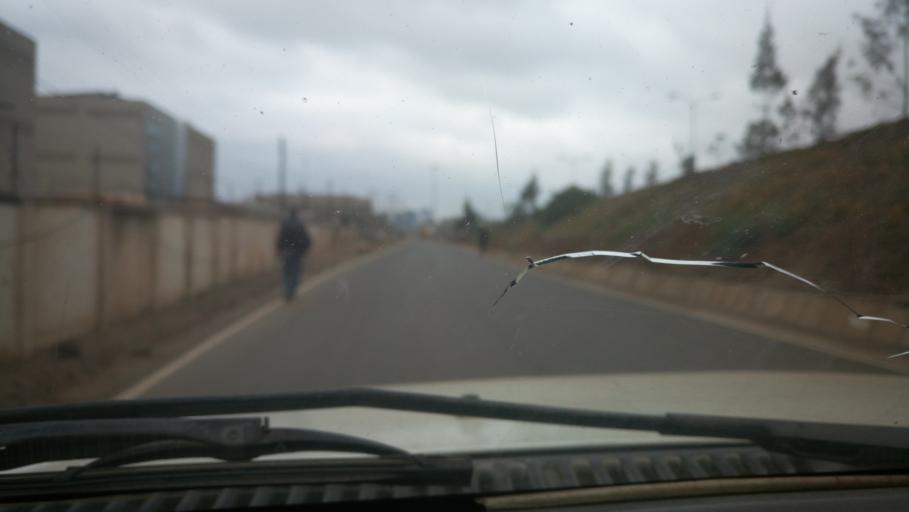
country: KE
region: Nairobi Area
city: Pumwani
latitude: -1.3323
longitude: 36.8876
